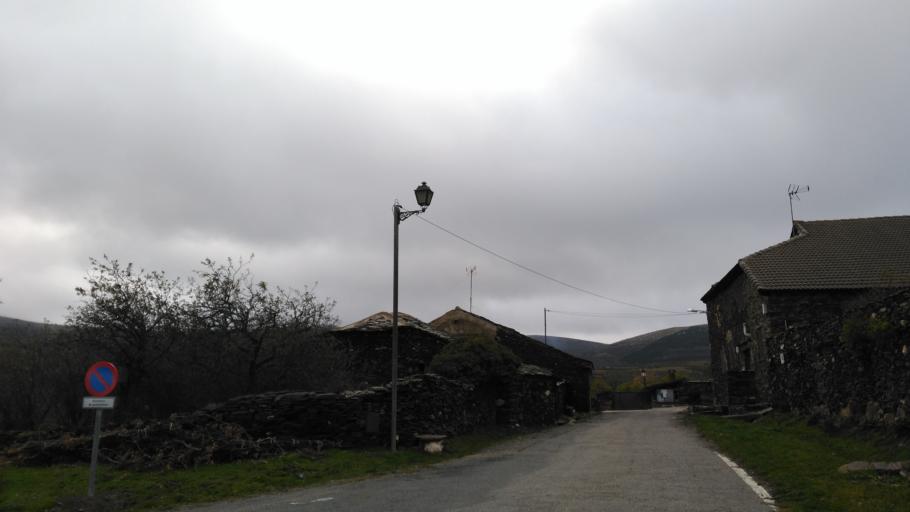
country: ES
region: Castille-La Mancha
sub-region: Provincia de Guadalajara
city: Cantalojas
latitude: 41.2843
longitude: -3.3161
